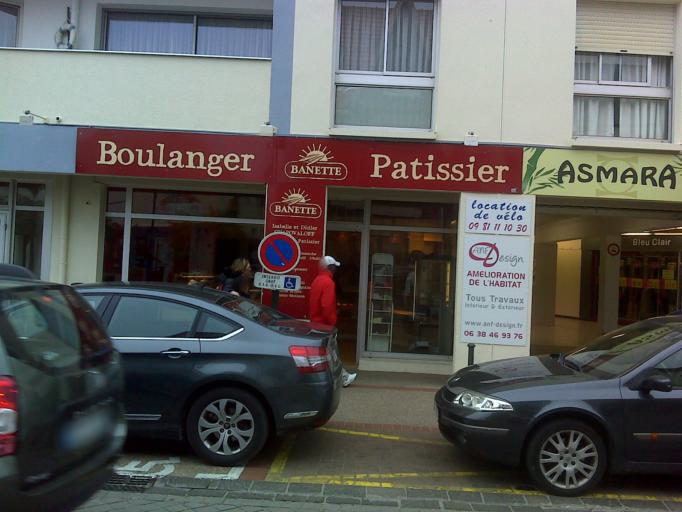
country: FR
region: Pays de la Loire
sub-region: Departement de la Loire-Atlantique
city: La Bernerie-en-Retz
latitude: 47.0806
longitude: -2.0377
